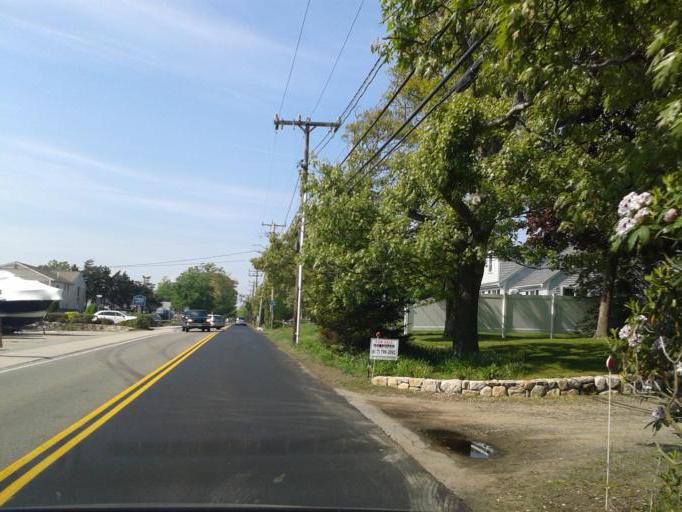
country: US
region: Massachusetts
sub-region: Barnstable County
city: Teaticket
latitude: 41.5515
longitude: -70.6000
